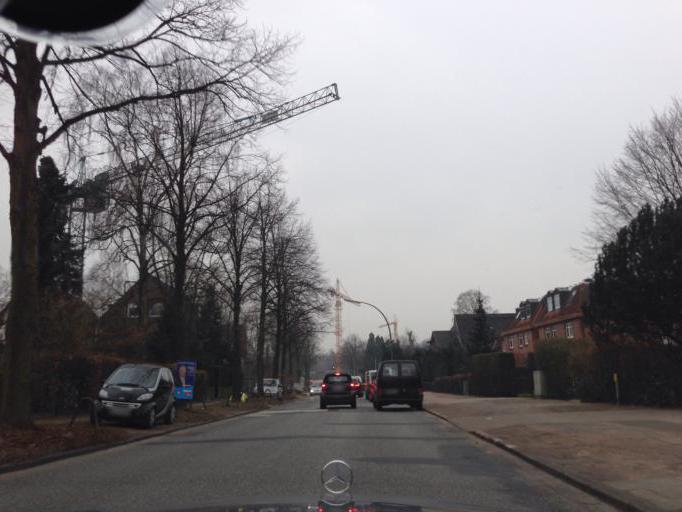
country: DE
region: Hamburg
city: Farmsen-Berne
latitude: 53.5970
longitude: 10.1231
